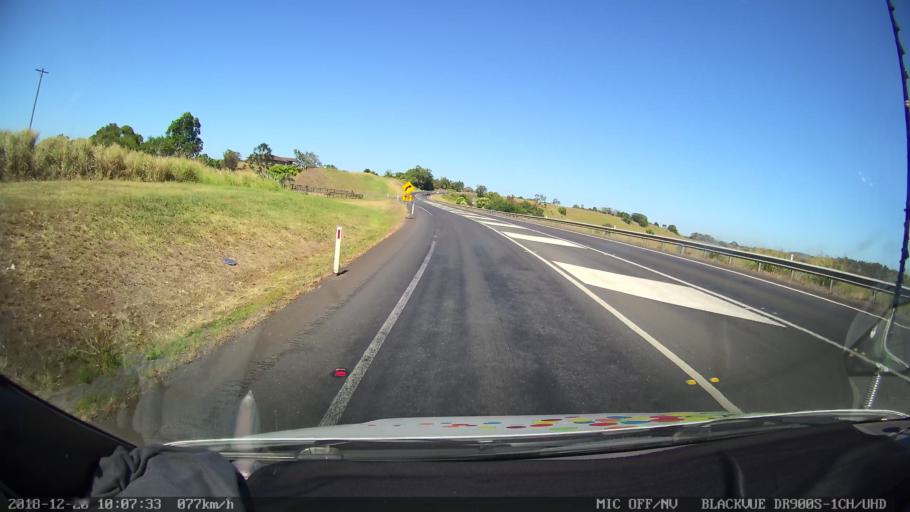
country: AU
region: New South Wales
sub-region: Lismore Municipality
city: Lismore
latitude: -28.8832
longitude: 153.2113
